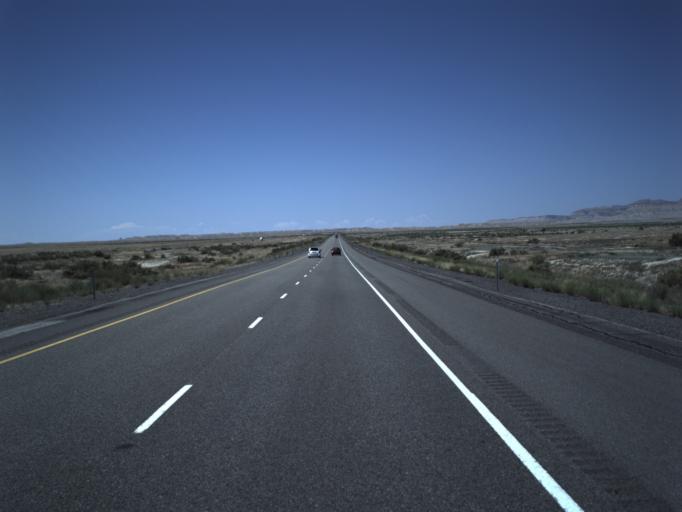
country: US
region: Utah
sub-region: Grand County
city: Moab
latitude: 38.9427
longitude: -109.5560
